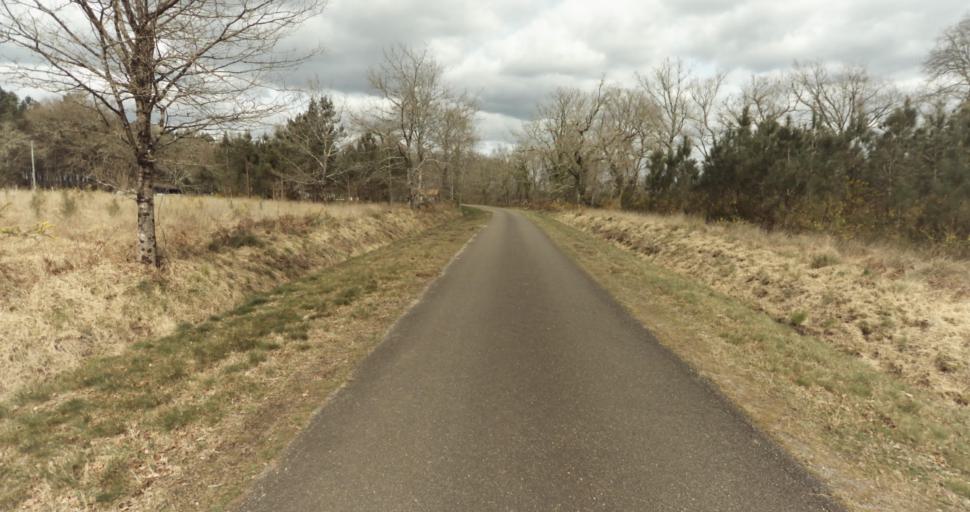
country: FR
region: Aquitaine
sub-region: Departement des Landes
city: Roquefort
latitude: 44.0939
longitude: -0.4540
